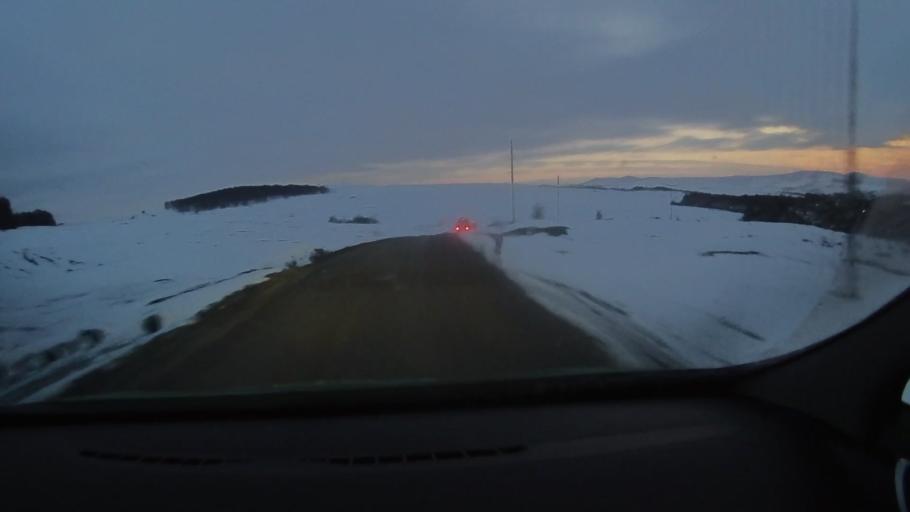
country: RO
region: Harghita
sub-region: Comuna Darjiu
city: Darjiu
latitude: 46.1766
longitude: 25.2476
